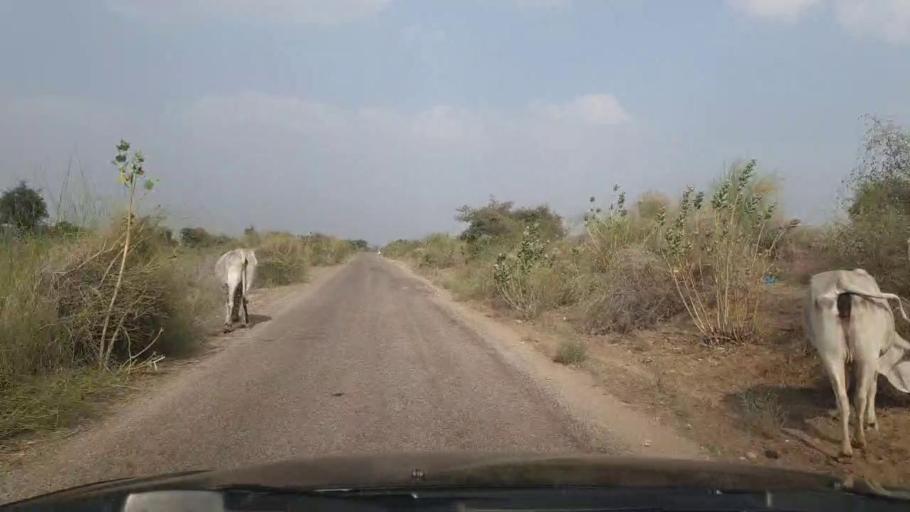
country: PK
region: Sindh
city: Islamkot
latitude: 25.0256
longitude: 70.5710
